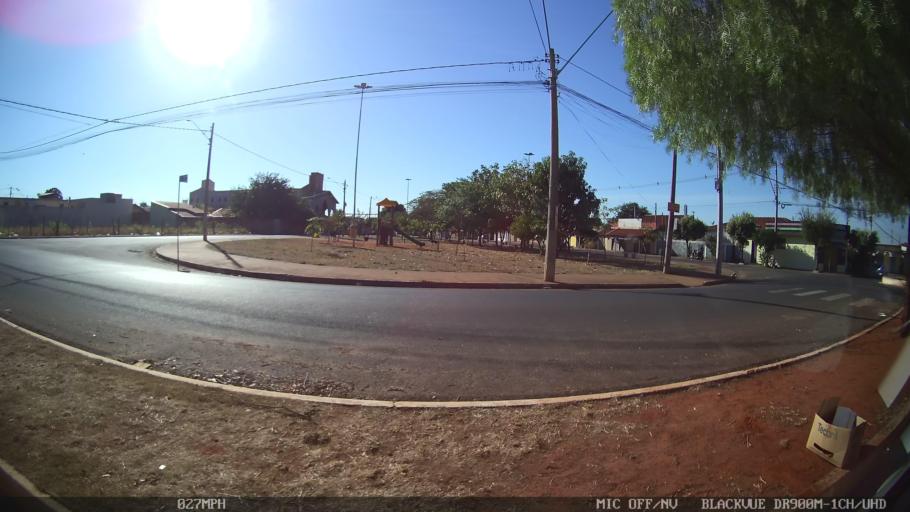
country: BR
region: Sao Paulo
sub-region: Olimpia
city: Olimpia
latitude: -20.7269
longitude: -48.8999
